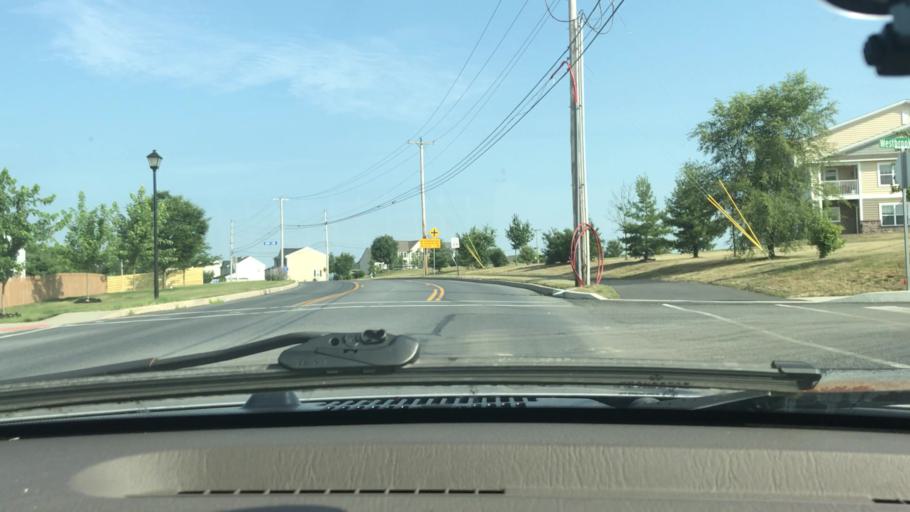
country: US
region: Pennsylvania
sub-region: Lancaster County
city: Rheems
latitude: 40.1413
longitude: -76.5653
